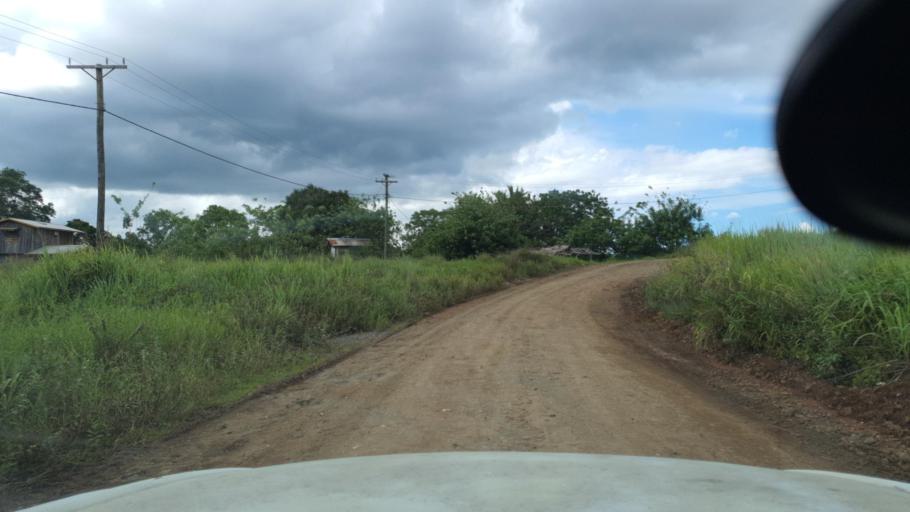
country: SB
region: Guadalcanal
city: Honiara
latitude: -9.5008
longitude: 160.1080
